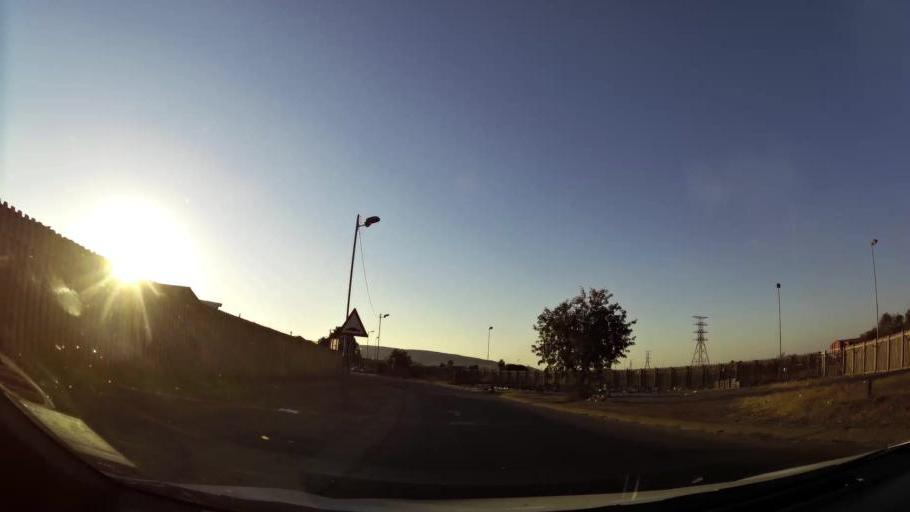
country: ZA
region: Gauteng
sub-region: City of Tshwane Metropolitan Municipality
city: Cullinan
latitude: -25.7203
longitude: 28.3973
